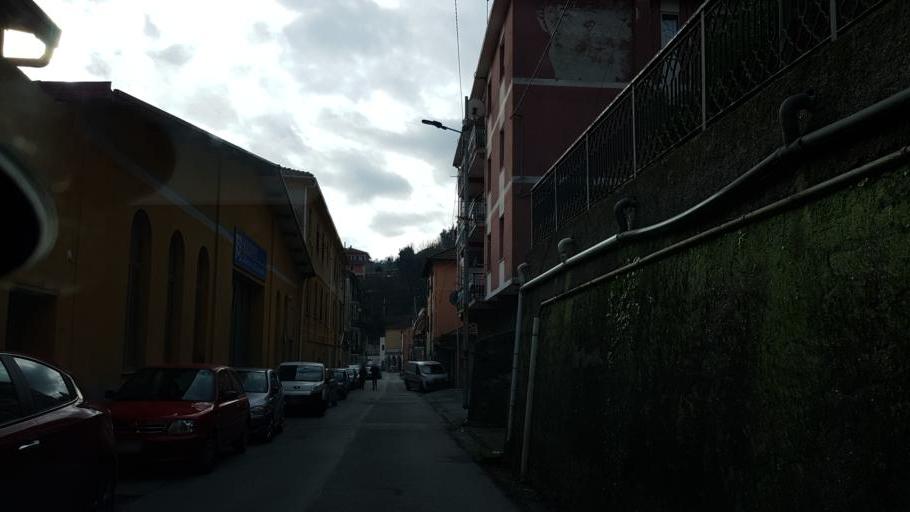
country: IT
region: Liguria
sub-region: Provincia di Genova
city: Santa Marta
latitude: 44.4763
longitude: 8.8875
